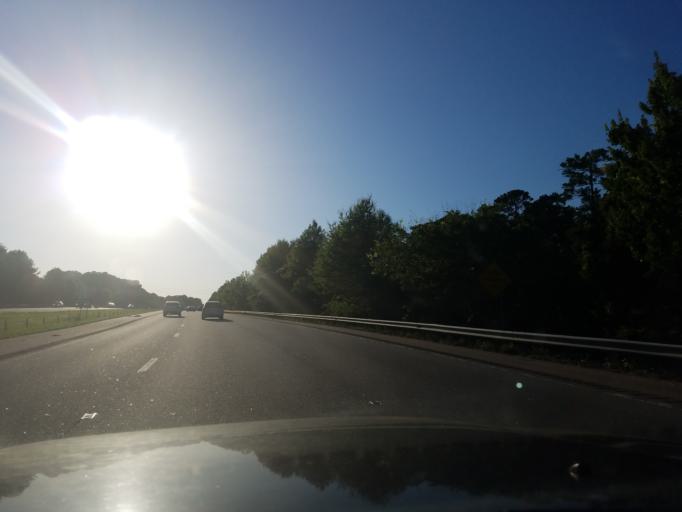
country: US
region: North Carolina
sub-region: Wake County
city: Wake Forest
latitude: 35.8928
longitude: -78.5975
